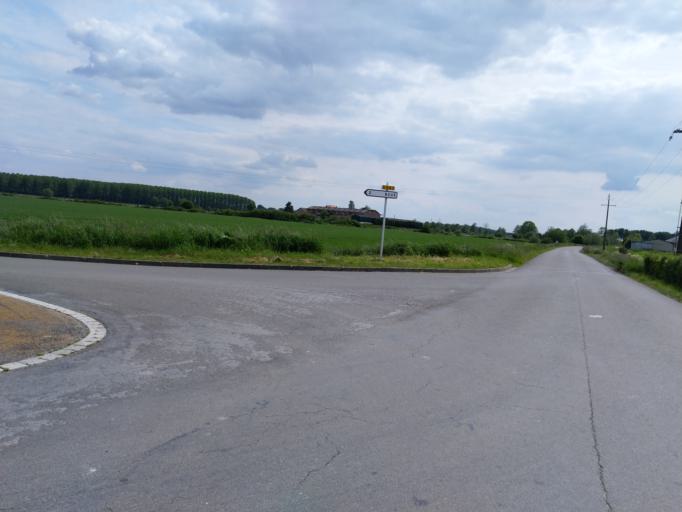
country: FR
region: Picardie
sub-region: Departement de l'Aisne
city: Boue
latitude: 50.0257
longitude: 3.6778
